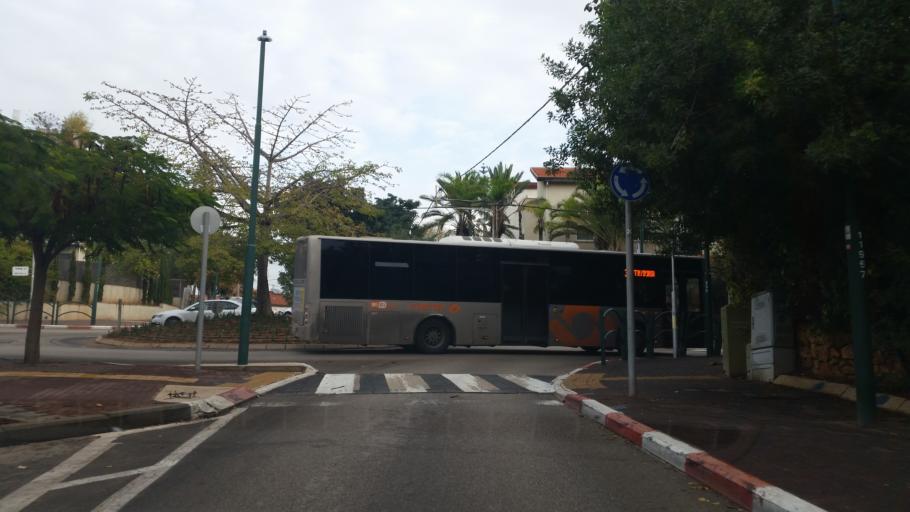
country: IL
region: Tel Aviv
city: Ramat HaSharon
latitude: 32.1590
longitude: 34.8501
